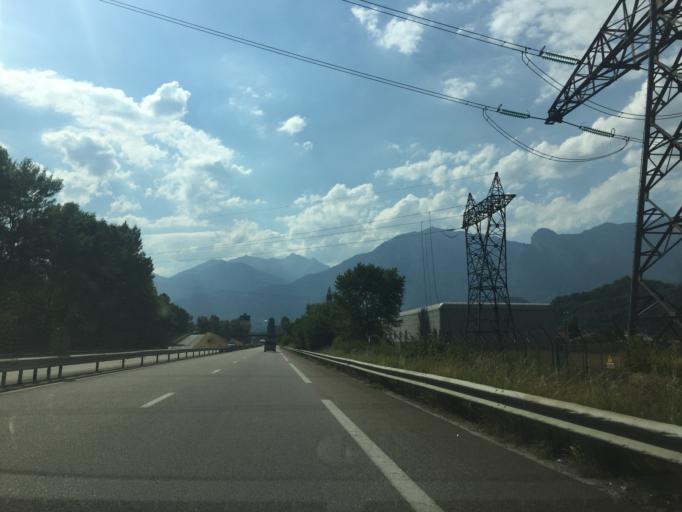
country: FR
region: Rhone-Alpes
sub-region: Departement de la Savoie
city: Albertville
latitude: 45.6612
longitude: 6.4148
